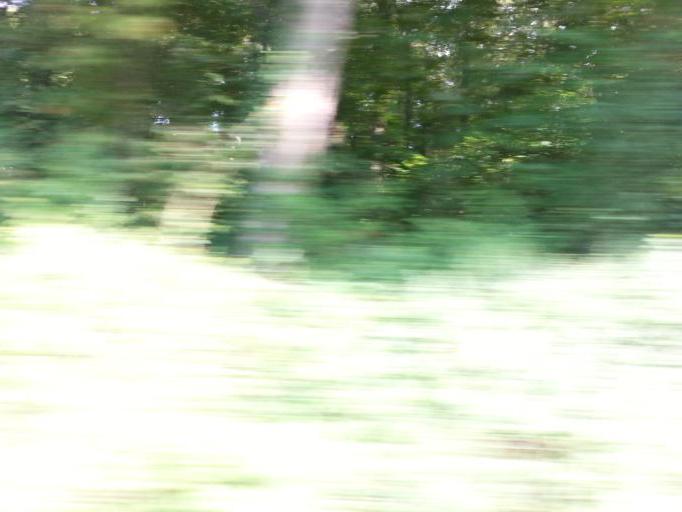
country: US
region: Tennessee
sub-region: Knox County
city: Knoxville
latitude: 36.0534
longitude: -83.8729
